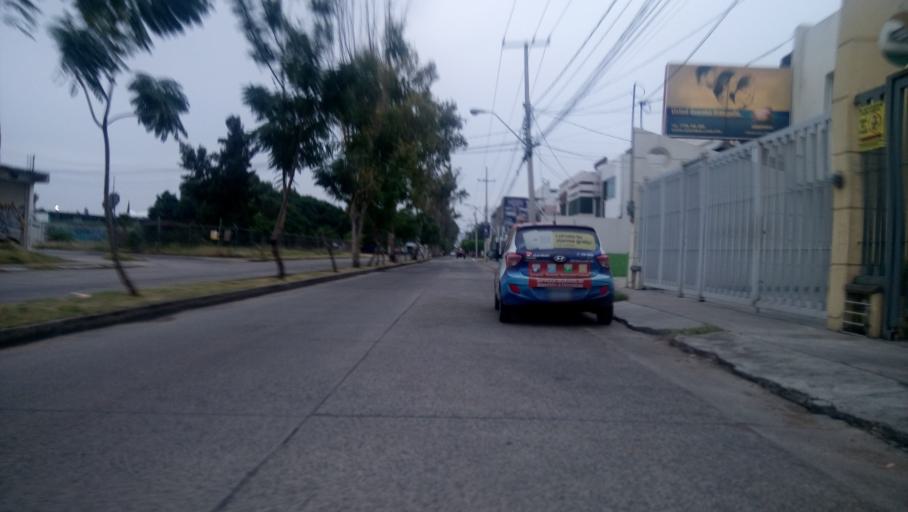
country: MX
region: Guanajuato
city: Leon
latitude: 21.1415
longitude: -101.6610
